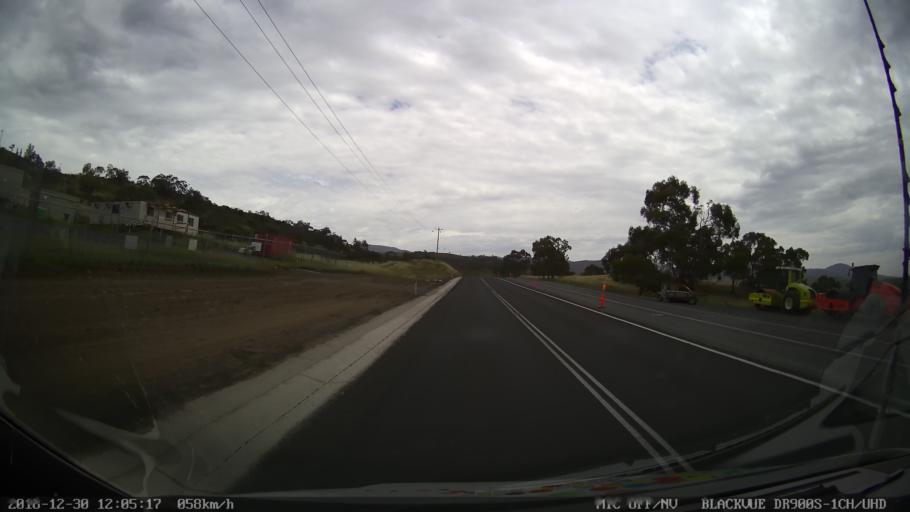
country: AU
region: New South Wales
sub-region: Snowy River
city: Jindabyne
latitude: -36.4139
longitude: 148.6068
